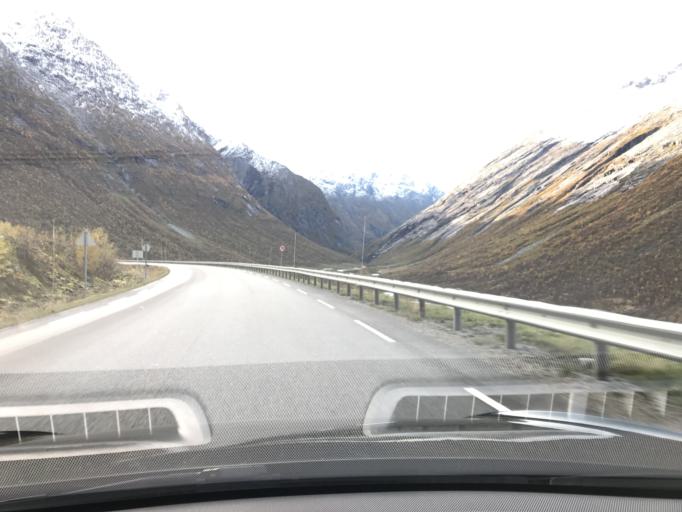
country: NO
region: More og Romsdal
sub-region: Norddal
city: Valldal
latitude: 61.9705
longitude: 7.2460
